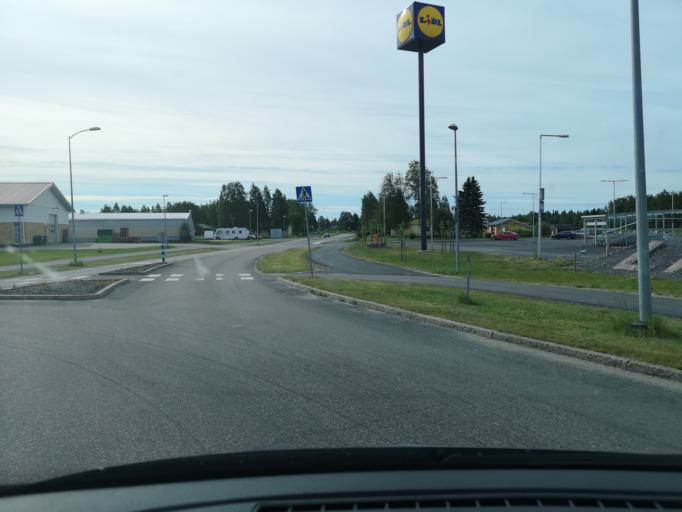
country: FI
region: Northern Ostrobothnia
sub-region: Ylivieska
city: Ylivieska
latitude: 64.0631
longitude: 24.5485
